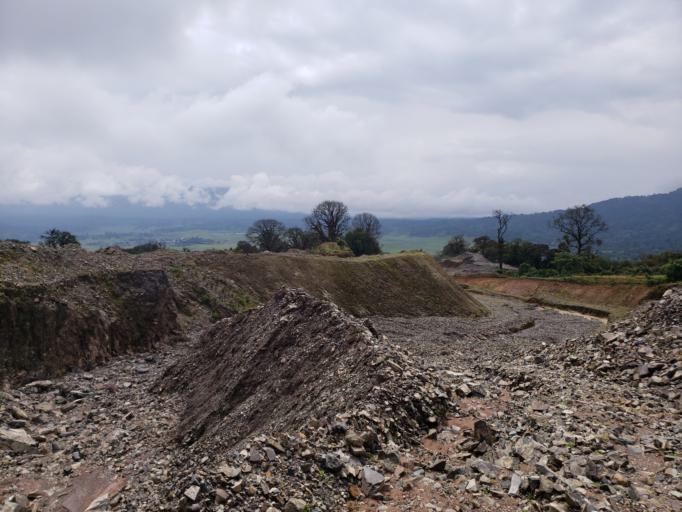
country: ET
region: Oromiya
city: Dodola
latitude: 6.6507
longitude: 39.3656
